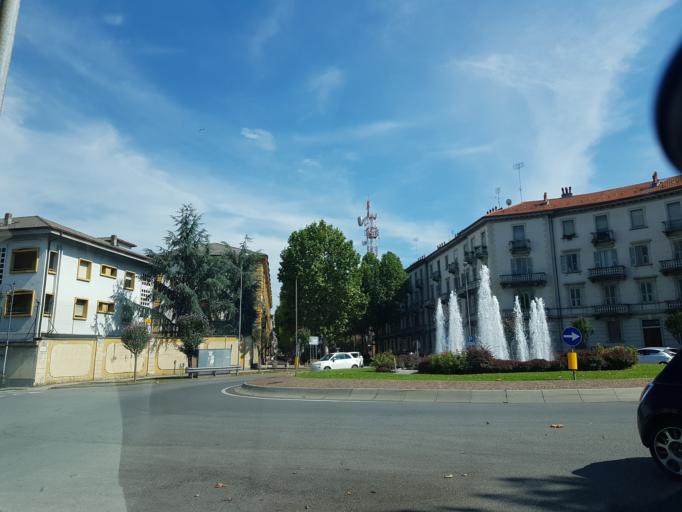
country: IT
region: Piedmont
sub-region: Provincia di Cuneo
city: Cuneo
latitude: 44.3912
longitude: 7.5427
